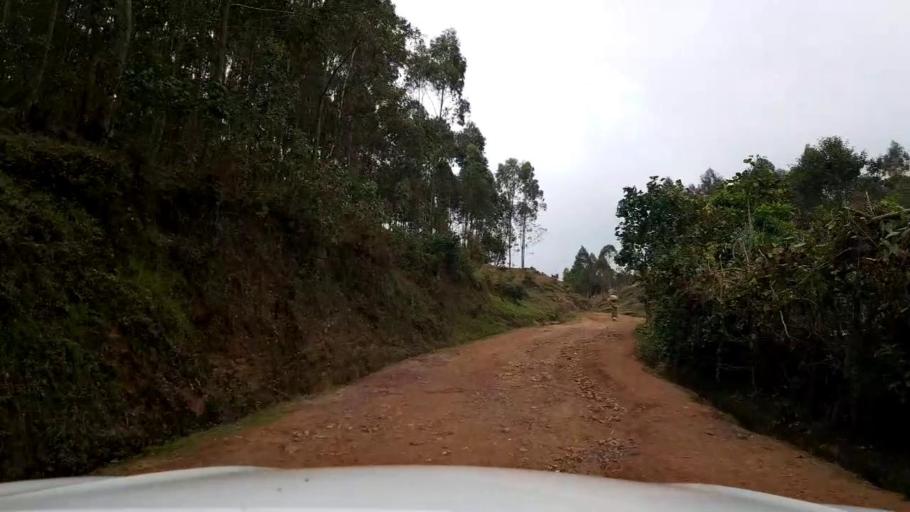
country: RW
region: Northern Province
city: Musanze
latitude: -1.6098
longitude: 29.7675
